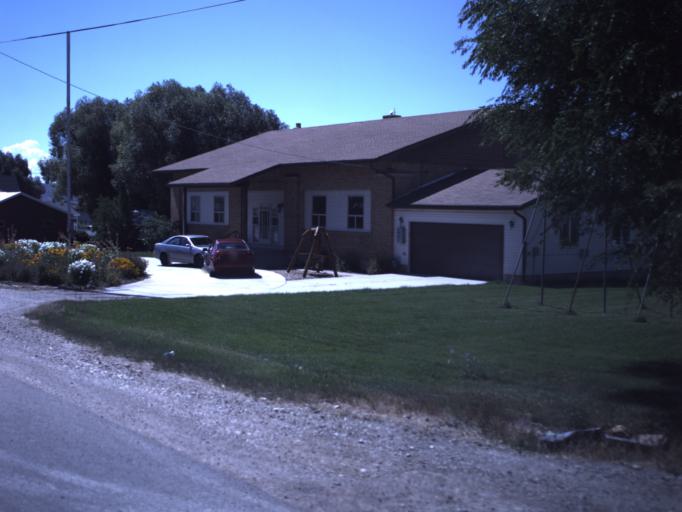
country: US
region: Utah
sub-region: Summit County
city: Kamas
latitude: 40.6774
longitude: -111.2809
